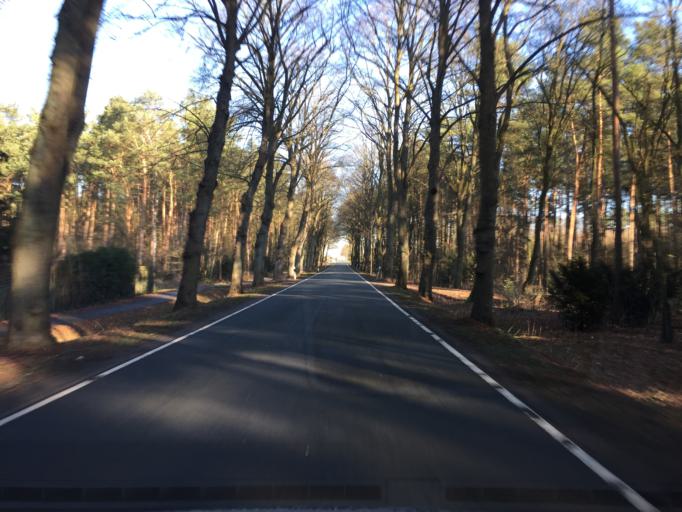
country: DE
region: Lower Saxony
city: Husum
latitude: 52.5583
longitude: 9.2415
